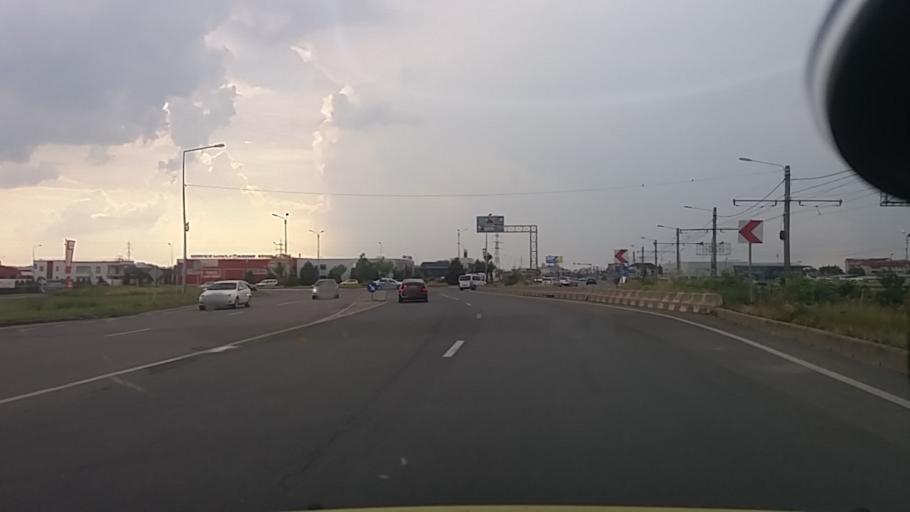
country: RO
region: Arad
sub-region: Comuna Vladimirescu
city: Vladimirescu
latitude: 46.1737
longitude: 21.3741
